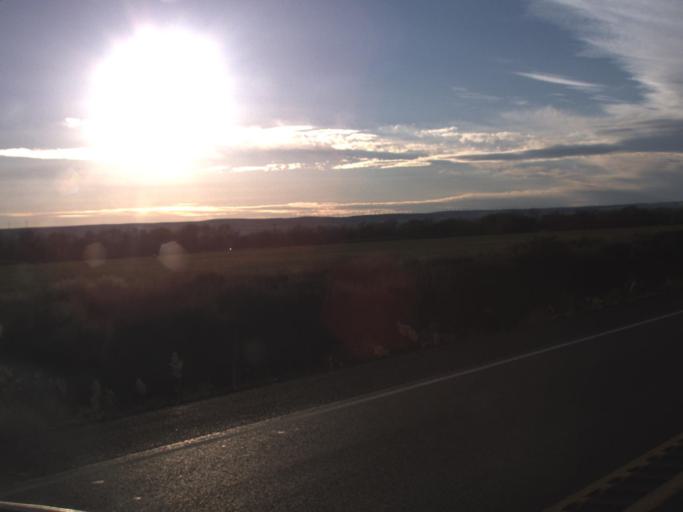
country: US
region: Washington
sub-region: Walla Walla County
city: Garrett
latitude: 46.0522
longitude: -118.5478
